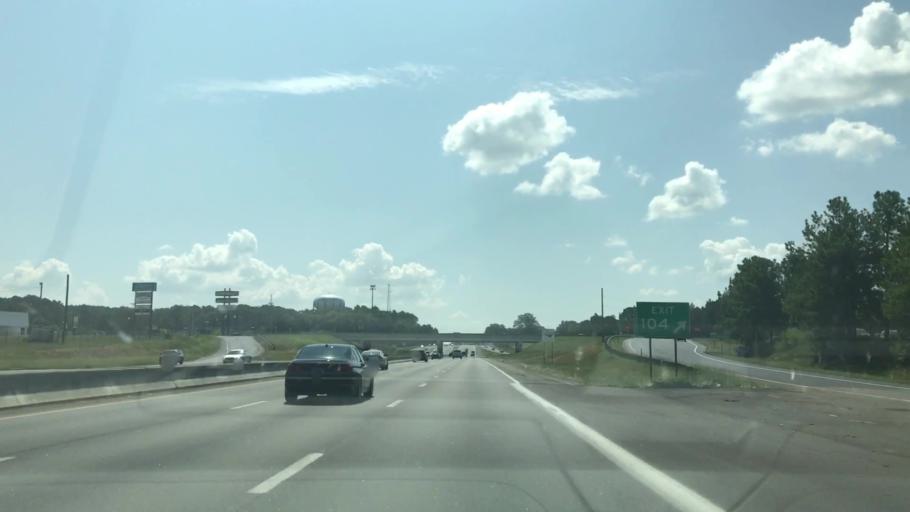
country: US
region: South Carolina
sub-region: Lexington County
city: Seven Oaks
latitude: 34.0685
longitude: -81.1442
